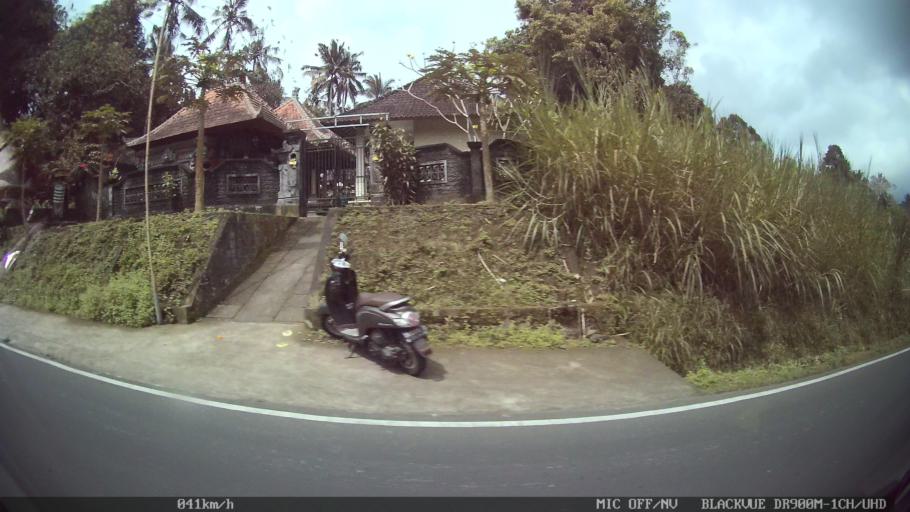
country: ID
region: Bali
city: Banjar Kubu
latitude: -8.4063
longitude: 115.4211
